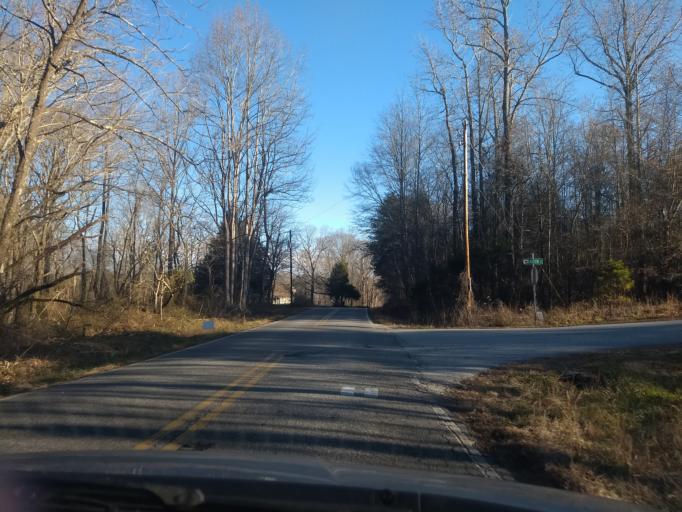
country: US
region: South Carolina
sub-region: Greenville County
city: Greer
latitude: 35.0132
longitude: -82.2080
